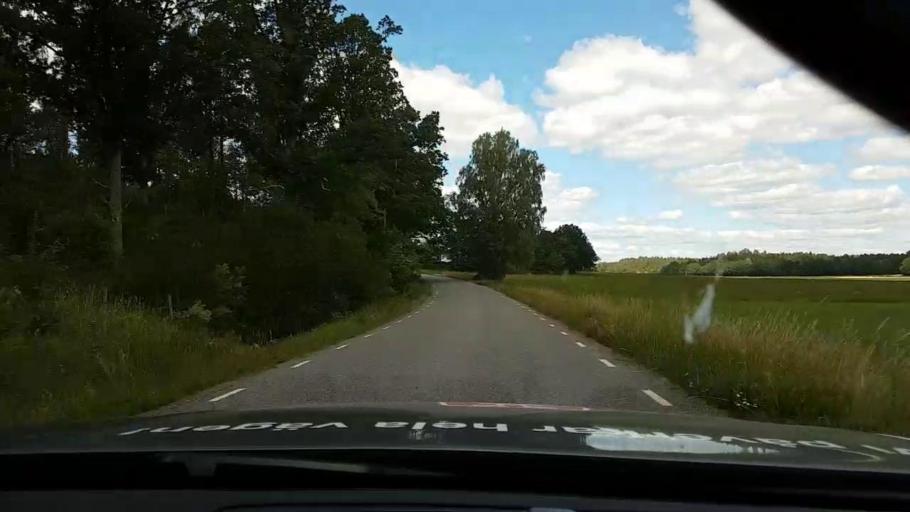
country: SE
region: Kalmar
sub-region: Vasterviks Kommun
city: Forserum
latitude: 57.9973
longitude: 16.5965
